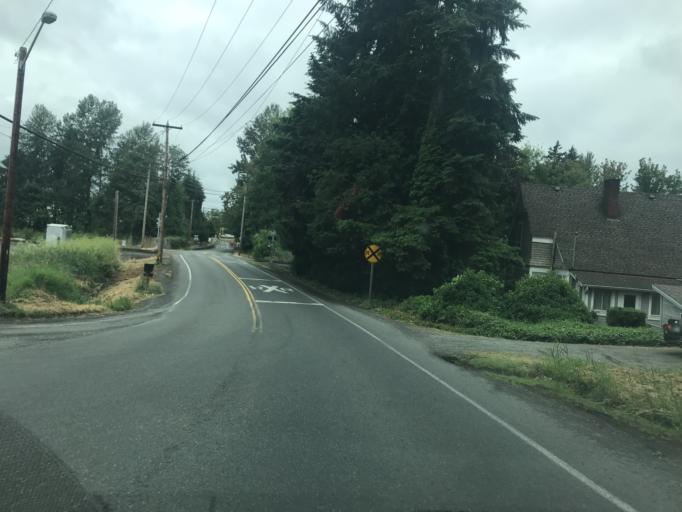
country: US
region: Washington
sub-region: King County
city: Covington
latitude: 47.3482
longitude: -122.1150
